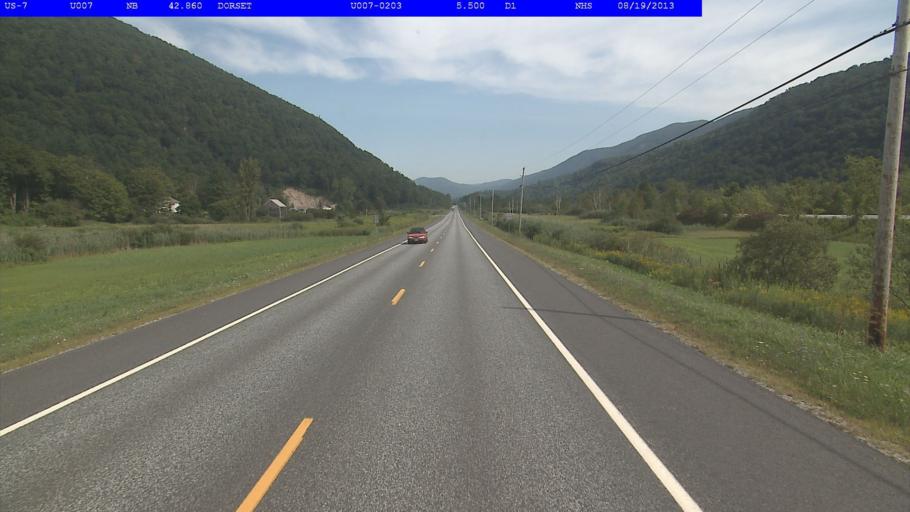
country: US
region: Vermont
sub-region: Bennington County
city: Manchester Center
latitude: 43.2878
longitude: -73.0007
